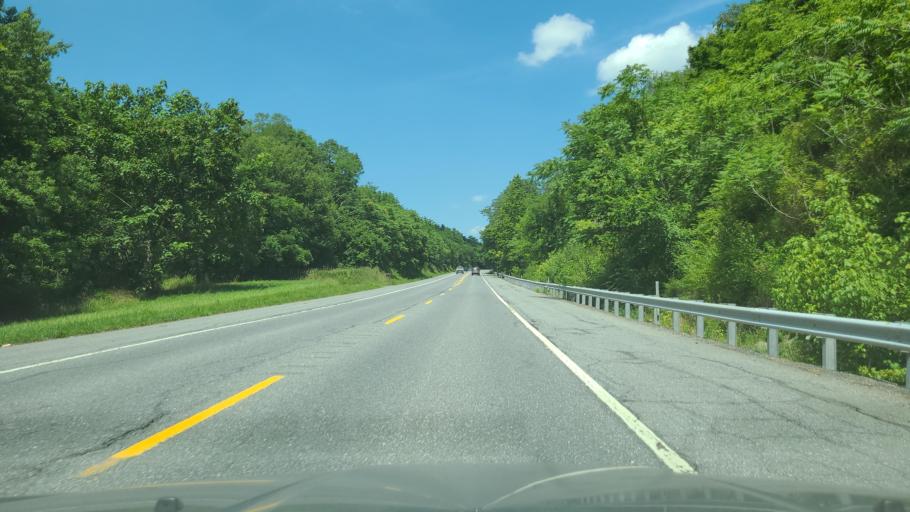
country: US
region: Maryland
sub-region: Frederick County
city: Middletown
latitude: 39.4288
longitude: -77.5555
